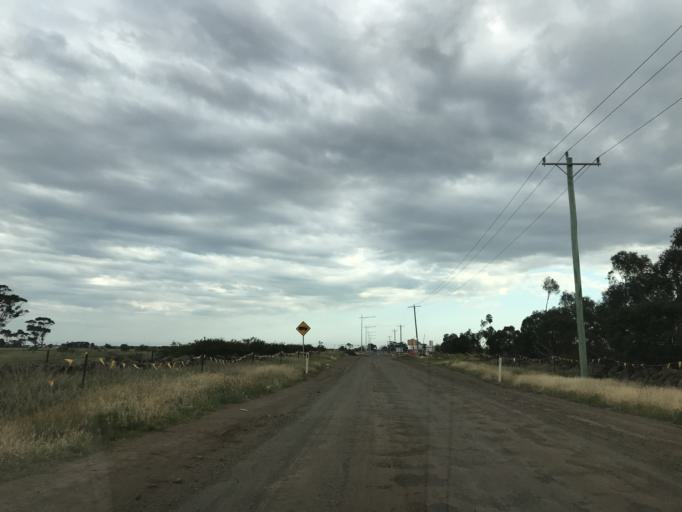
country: AU
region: Victoria
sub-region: Wyndham
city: Truganina
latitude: -37.8118
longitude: 144.7229
